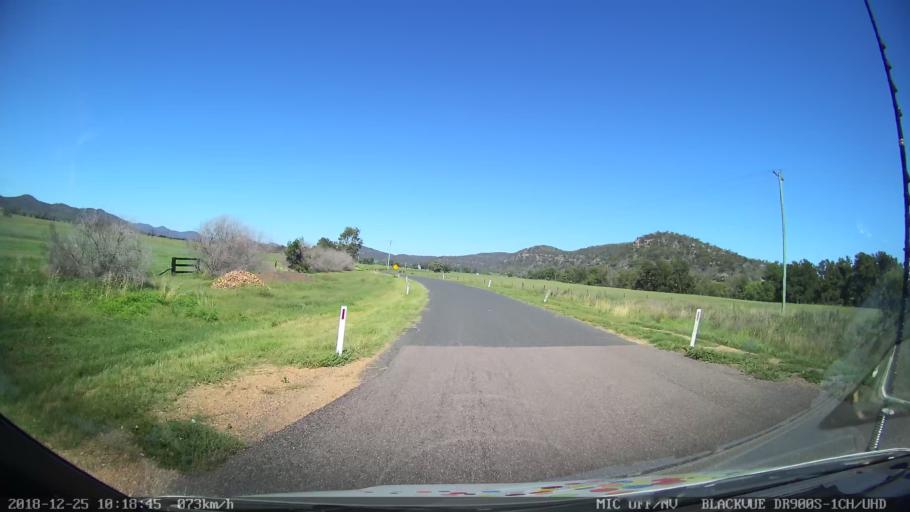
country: AU
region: New South Wales
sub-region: Muswellbrook
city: Denman
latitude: -32.3469
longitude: 150.5657
